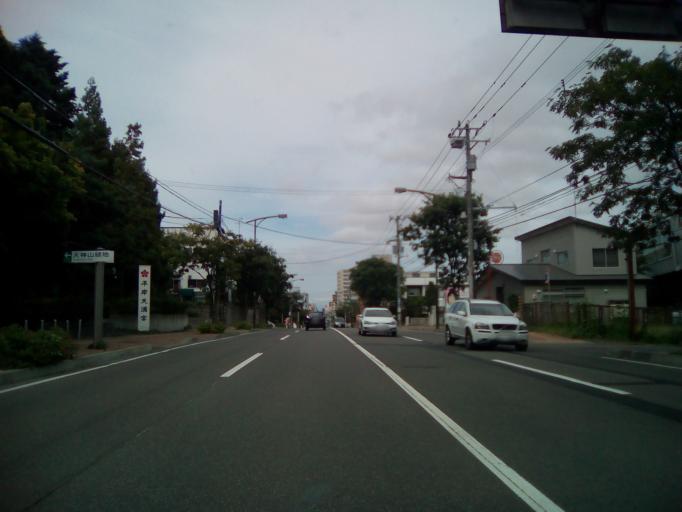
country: JP
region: Hokkaido
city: Sapporo
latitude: 43.0218
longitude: 141.3673
